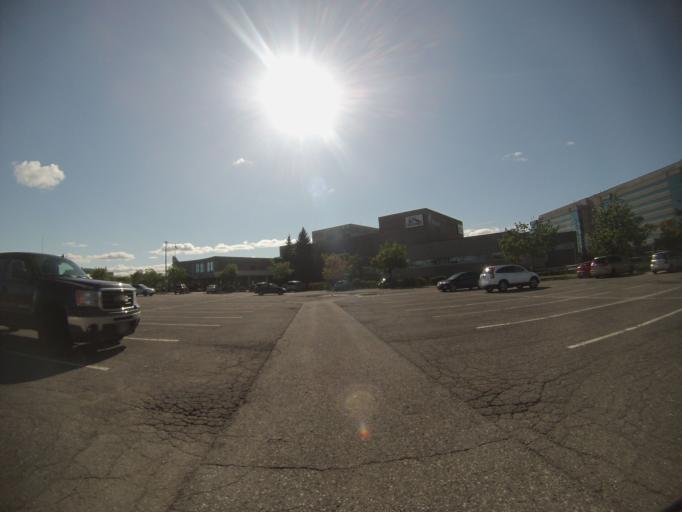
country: CA
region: Ontario
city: Bells Corners
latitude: 45.3450
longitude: -75.7614
